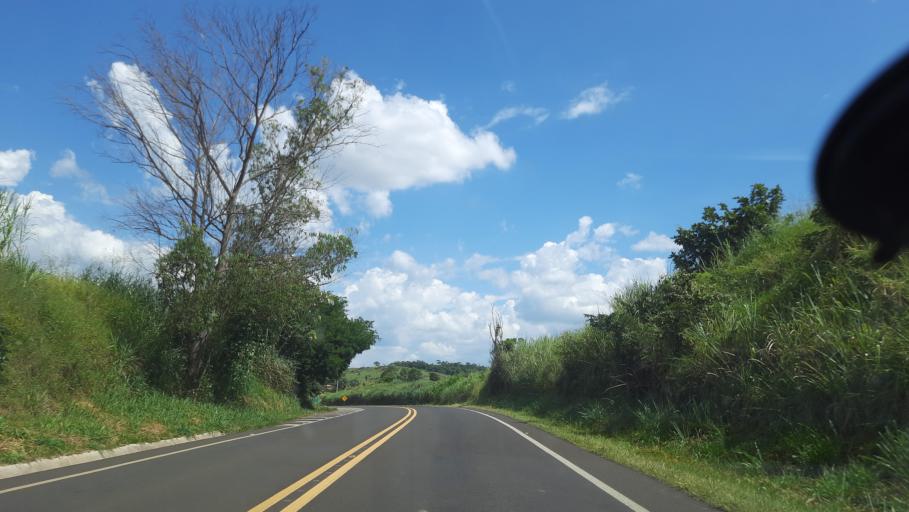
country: BR
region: Sao Paulo
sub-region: Sao Jose Do Rio Pardo
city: Sao Jose do Rio Pardo
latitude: -21.6036
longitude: -46.9381
